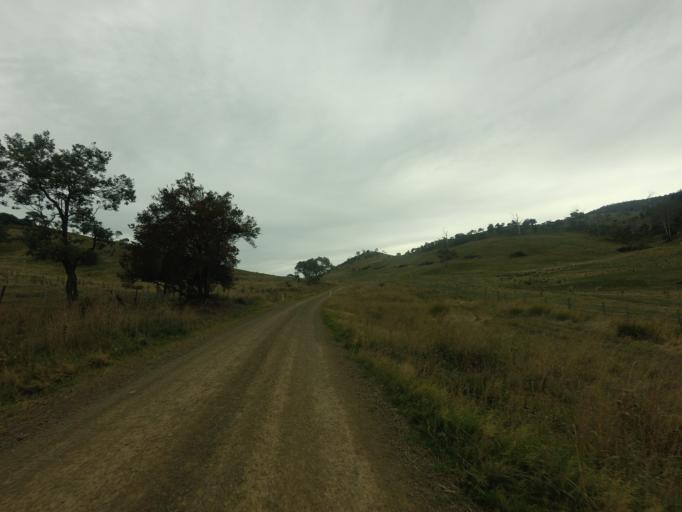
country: AU
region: Tasmania
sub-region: Derwent Valley
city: New Norfolk
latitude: -42.3766
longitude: 146.8644
